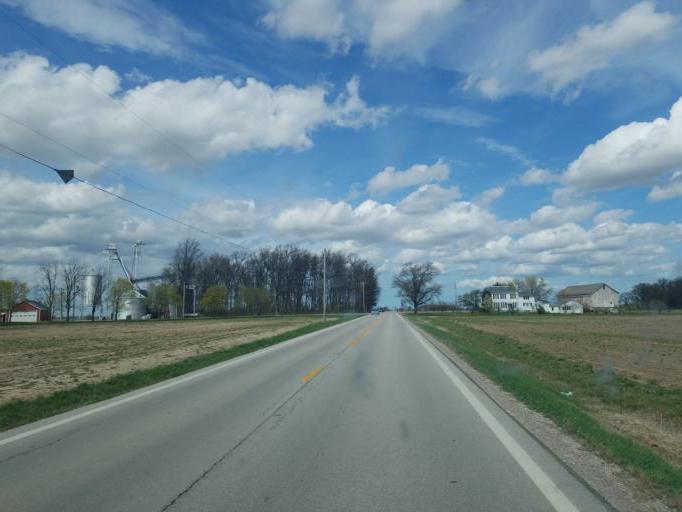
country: US
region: Ohio
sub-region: Huron County
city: Bellevue
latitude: 41.2461
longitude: -82.8035
